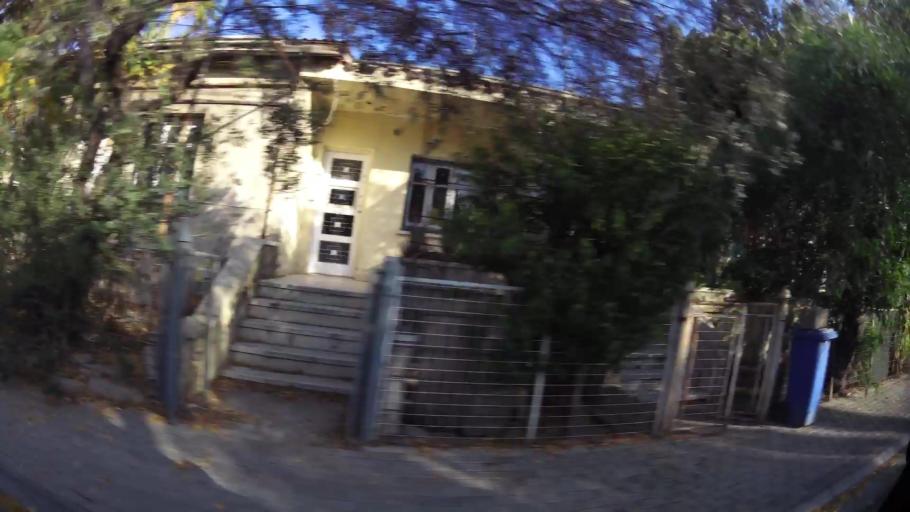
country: CY
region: Lefkosia
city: Nicosia
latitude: 35.1721
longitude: 33.3441
